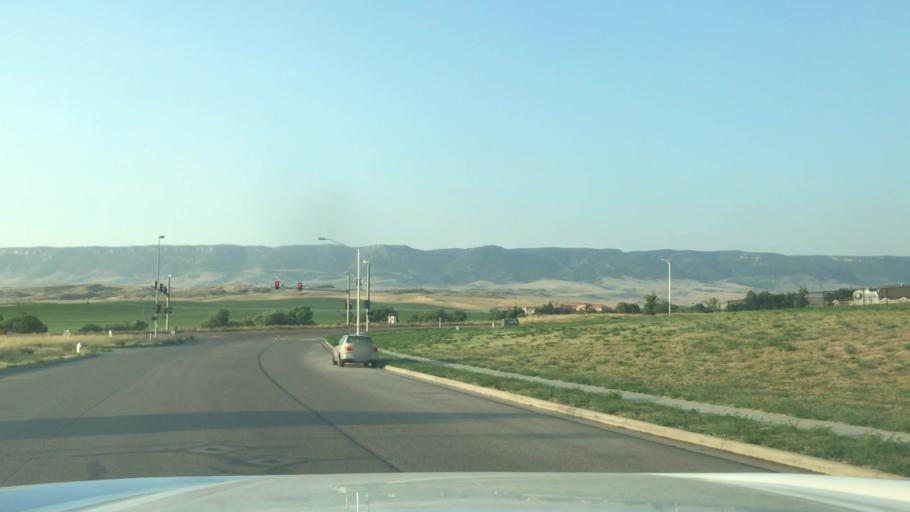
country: US
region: Wyoming
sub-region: Natrona County
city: Evansville
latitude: 42.8408
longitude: -106.2238
